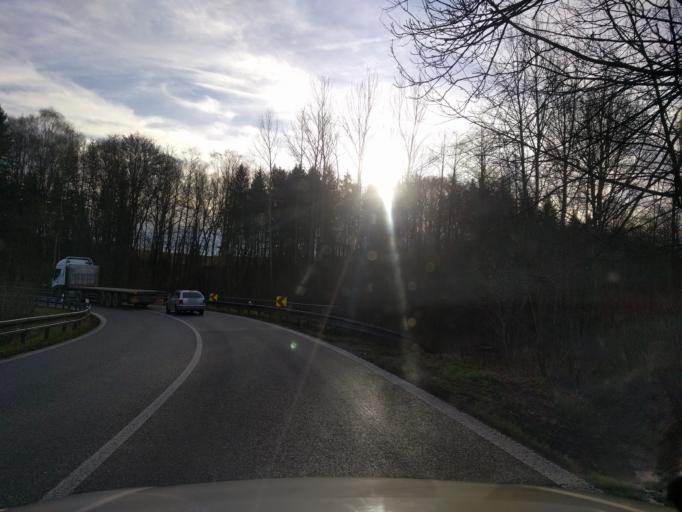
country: CZ
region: Liberecky
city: Mnisek
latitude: 50.8455
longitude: 15.0325
